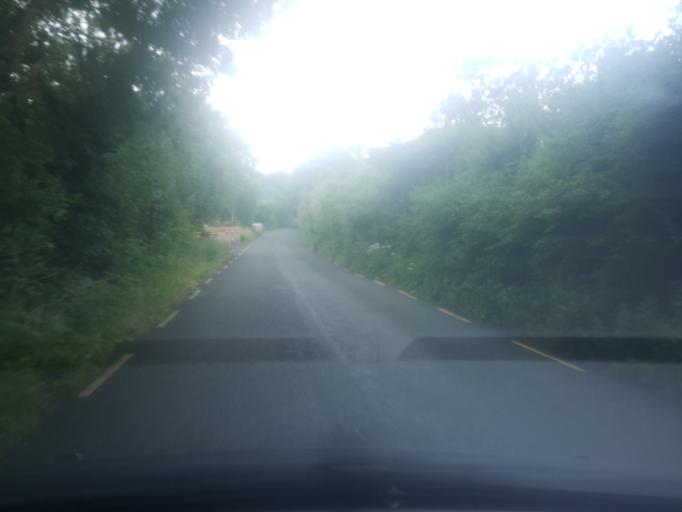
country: IE
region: Munster
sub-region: Ciarrai
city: Cill Airne
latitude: 52.0937
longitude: -9.4778
